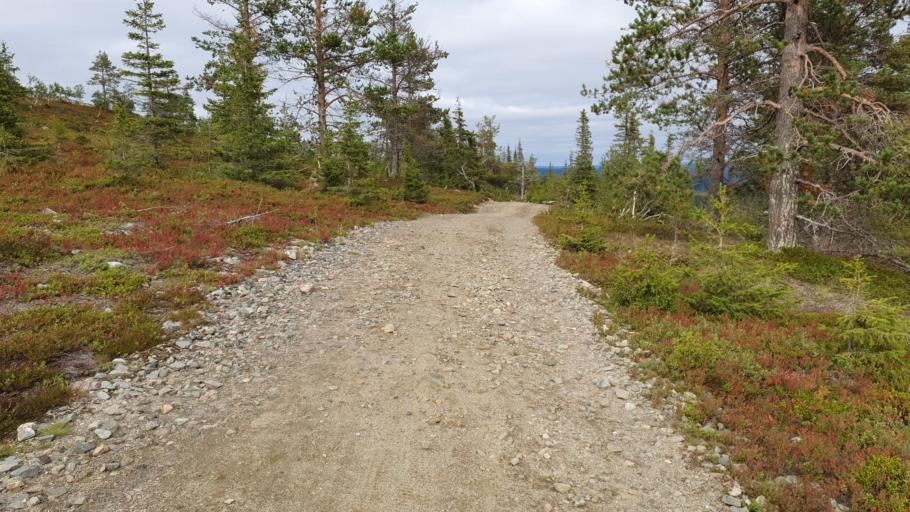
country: FI
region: Lapland
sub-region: Tunturi-Lappi
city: Kolari
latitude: 67.5642
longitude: 24.2573
